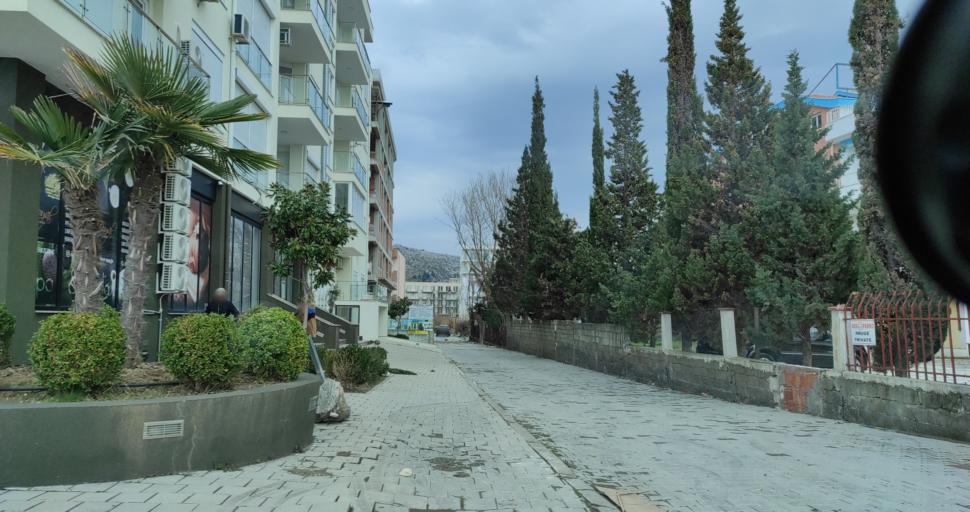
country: AL
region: Lezhe
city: Shengjin
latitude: 41.7963
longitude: 19.6020
